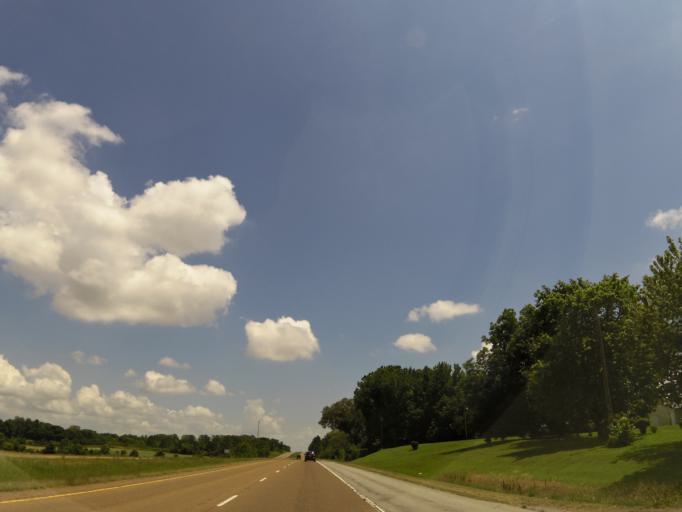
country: US
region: Tennessee
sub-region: Lauderdale County
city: Halls
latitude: 35.9168
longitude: -89.2720
